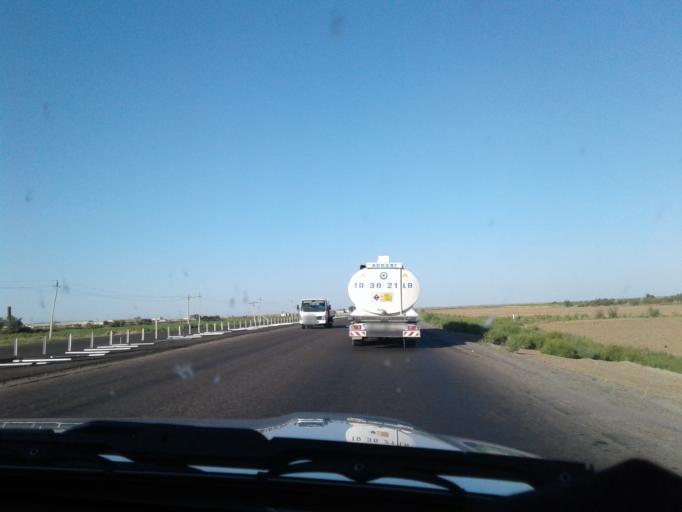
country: TM
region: Mary
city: Mary
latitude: 37.2606
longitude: 61.2591
